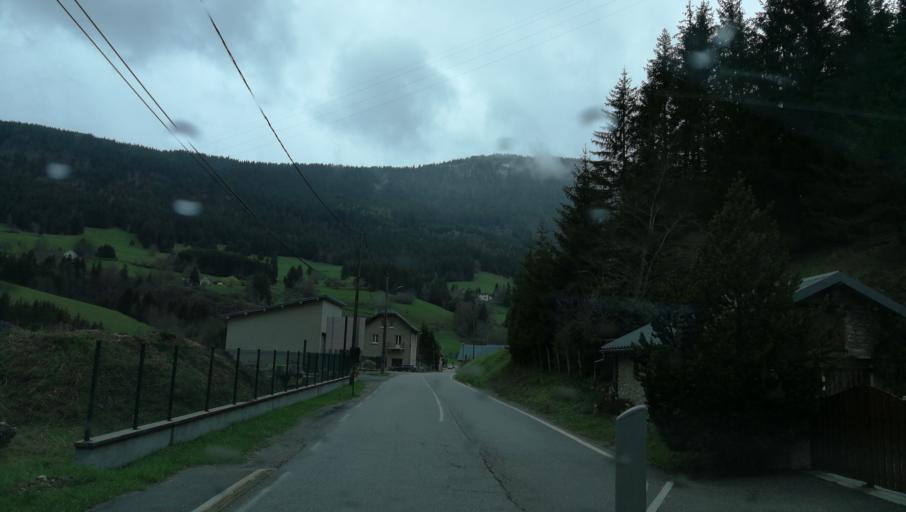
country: FR
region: Rhone-Alpes
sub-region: Departement de l'Isere
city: Villard-de-Lans
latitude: 45.0848
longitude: 5.5286
